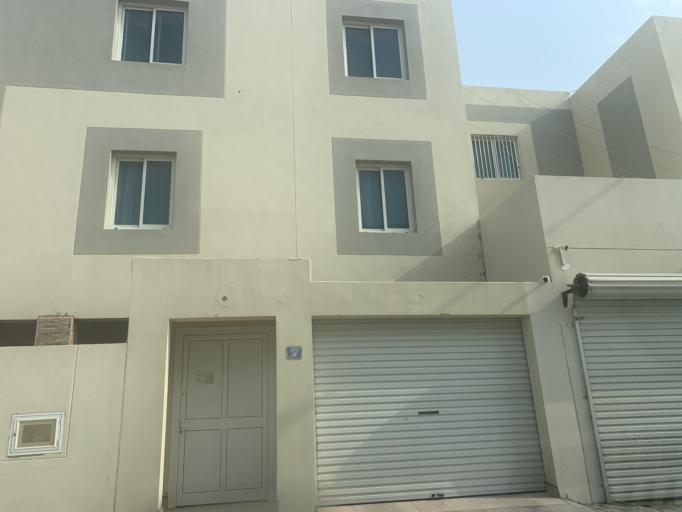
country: BH
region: Manama
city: Jidd Hafs
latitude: 26.2292
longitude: 50.4574
